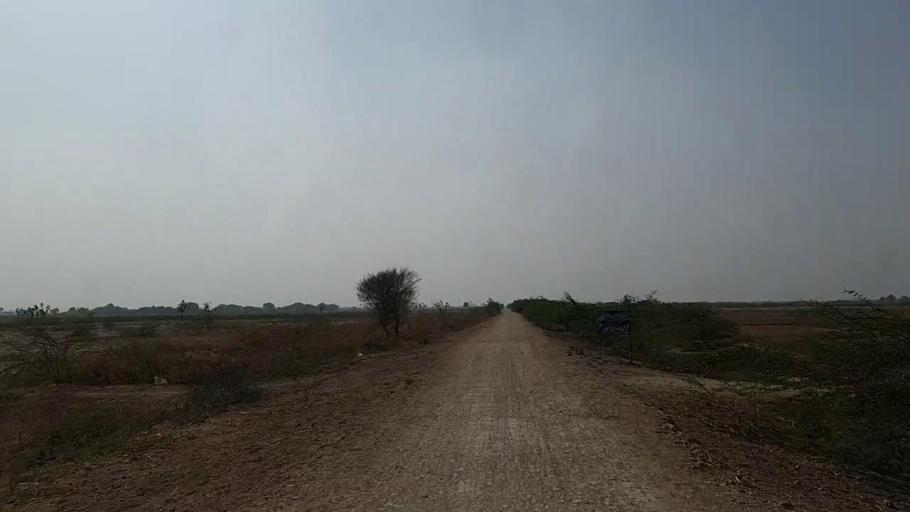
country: PK
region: Sindh
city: Naukot
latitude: 24.7605
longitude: 69.3306
